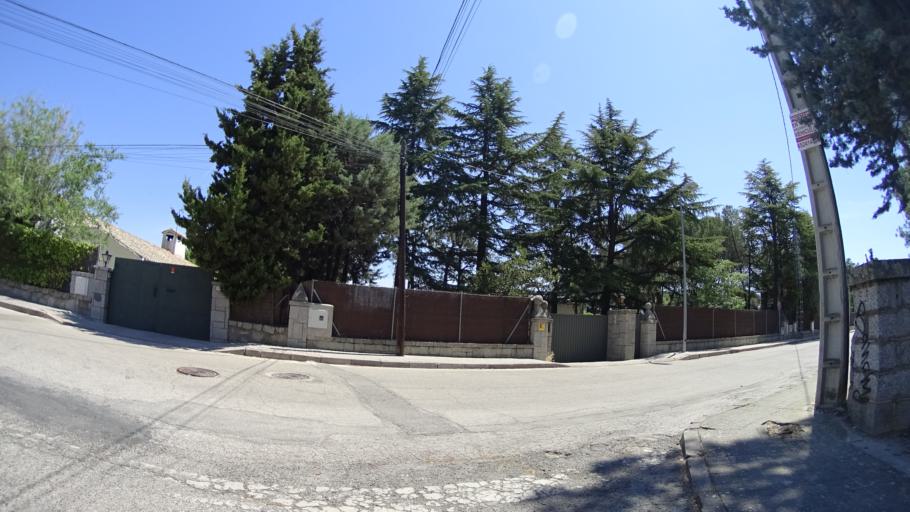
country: ES
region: Madrid
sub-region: Provincia de Madrid
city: Colmenarejo
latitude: 40.5567
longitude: -4.0070
